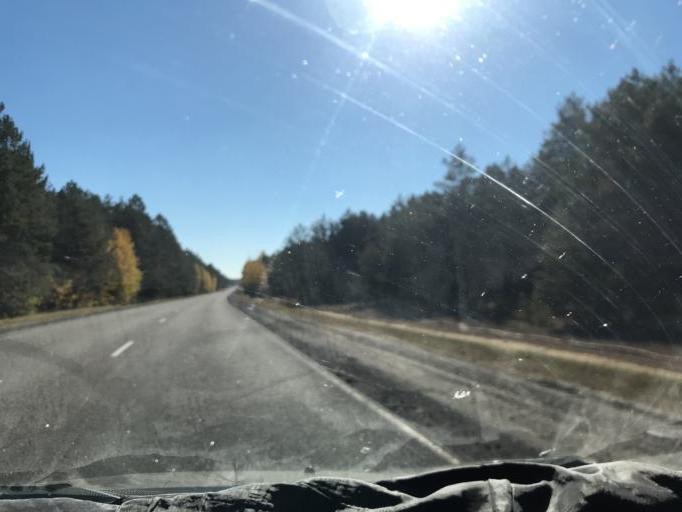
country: BY
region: Gomel
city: Kalinkavichy
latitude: 52.4453
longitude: 29.2768
